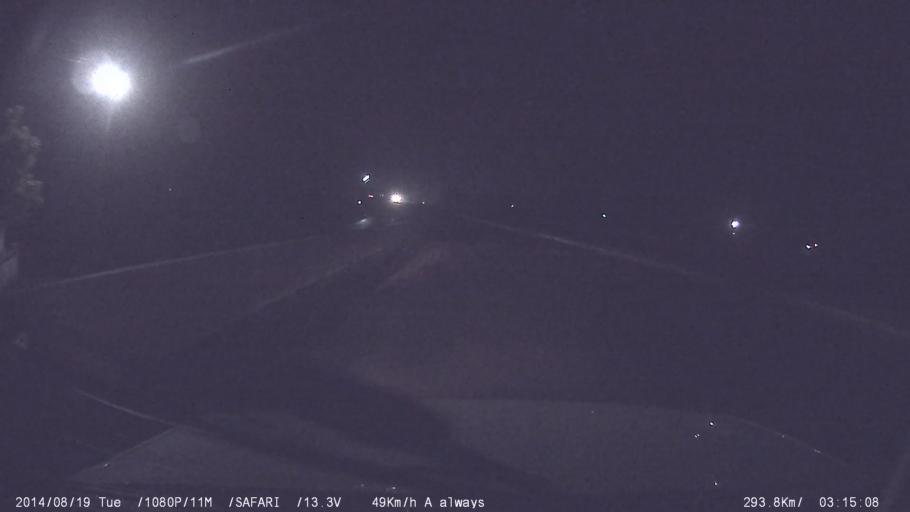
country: IN
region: Tamil Nadu
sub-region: Coimbatore
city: Sulur
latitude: 11.1096
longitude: 77.1795
